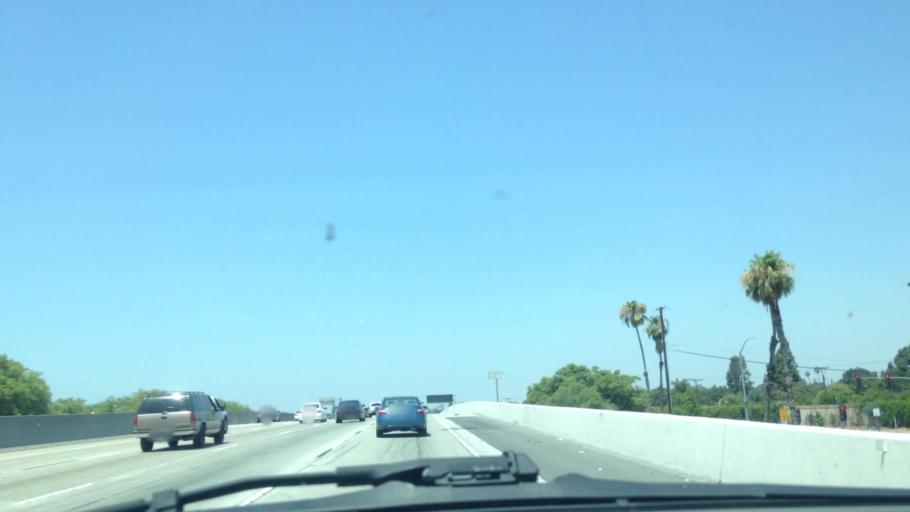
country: US
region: California
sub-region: Orange County
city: Fullerton
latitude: 33.8544
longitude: -117.9410
